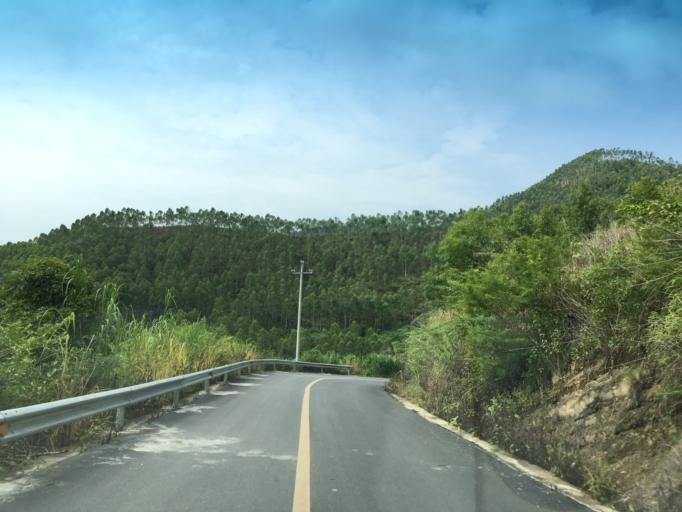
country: CN
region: Guangxi Zhuangzu Zizhiqu
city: Xinzhou
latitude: 24.8187
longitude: 105.6467
